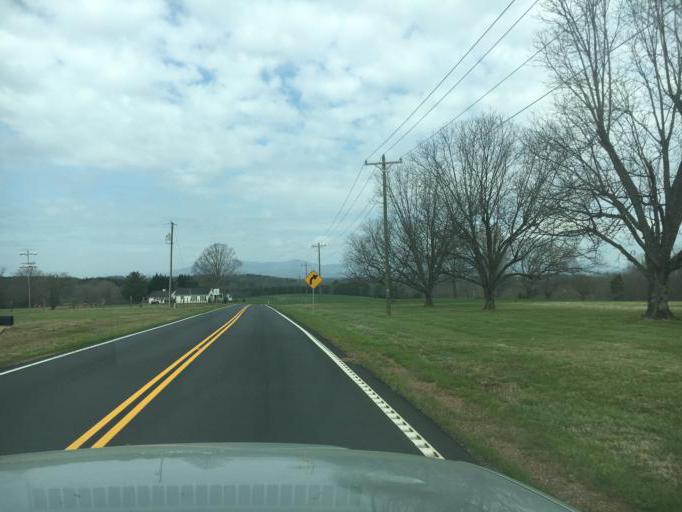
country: US
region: South Carolina
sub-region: Spartanburg County
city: Inman Mills
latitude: 35.0793
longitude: -82.1855
